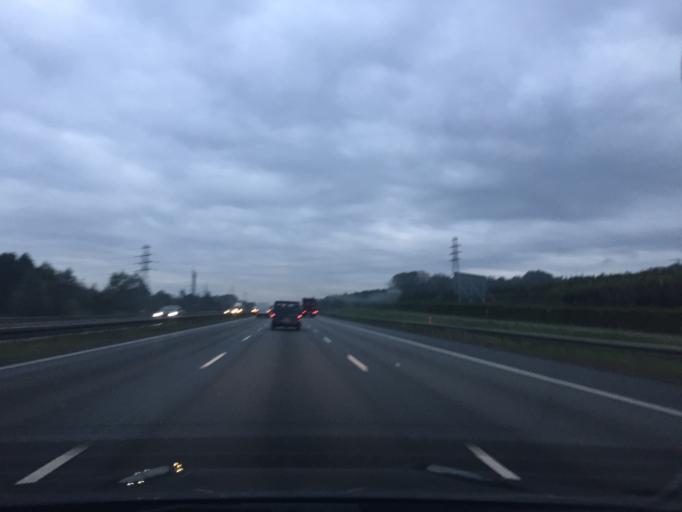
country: PL
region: Lesser Poland Voivodeship
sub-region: Powiat krakowski
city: Ochojno
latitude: 50.0013
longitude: 19.9781
